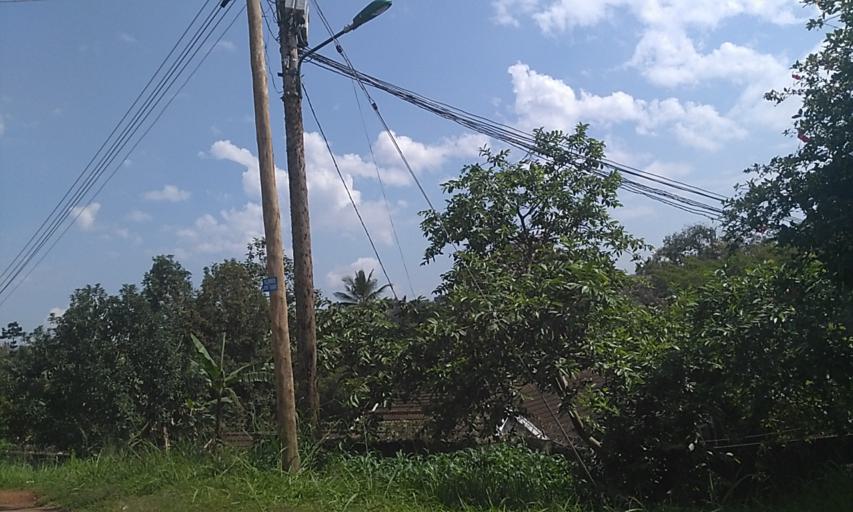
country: UG
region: Central Region
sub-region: Wakiso District
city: Kireka
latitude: 0.3540
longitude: 32.6210
